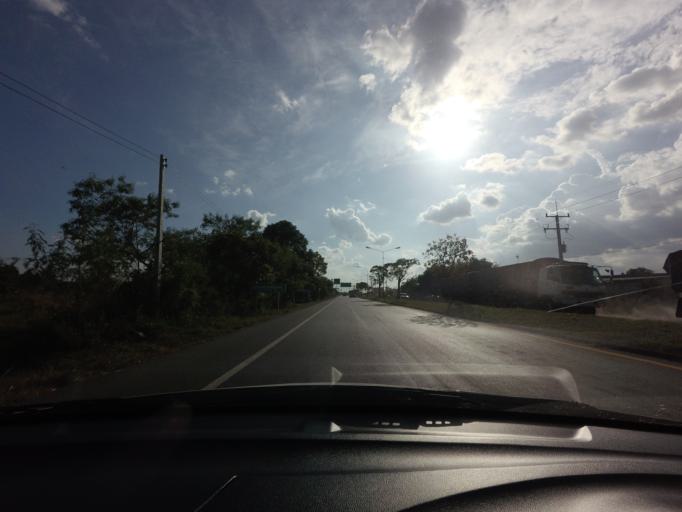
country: TH
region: Nakhon Nayok
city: Nakhon Nayok
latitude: 14.2284
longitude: 101.1795
